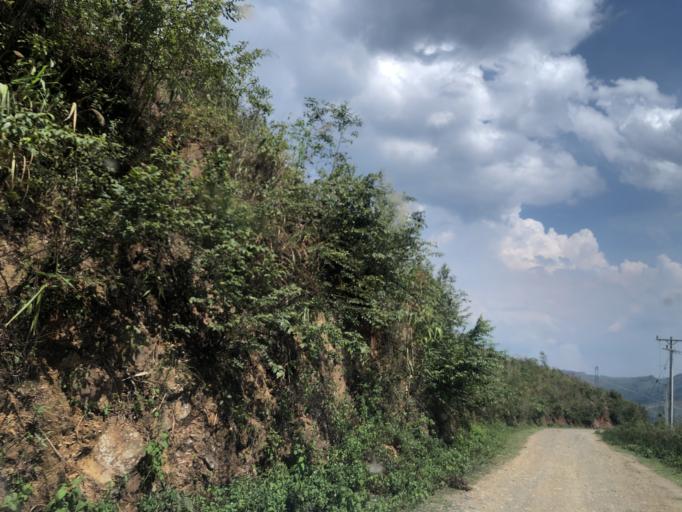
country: LA
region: Phongsali
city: Phongsali
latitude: 21.4084
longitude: 102.2370
